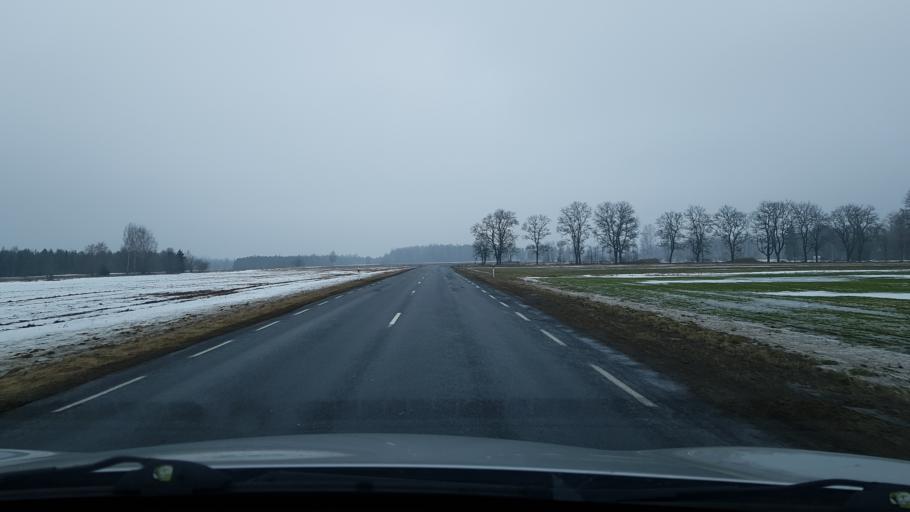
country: EE
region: Valgamaa
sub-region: Torva linn
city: Torva
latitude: 58.1894
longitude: 25.9514
